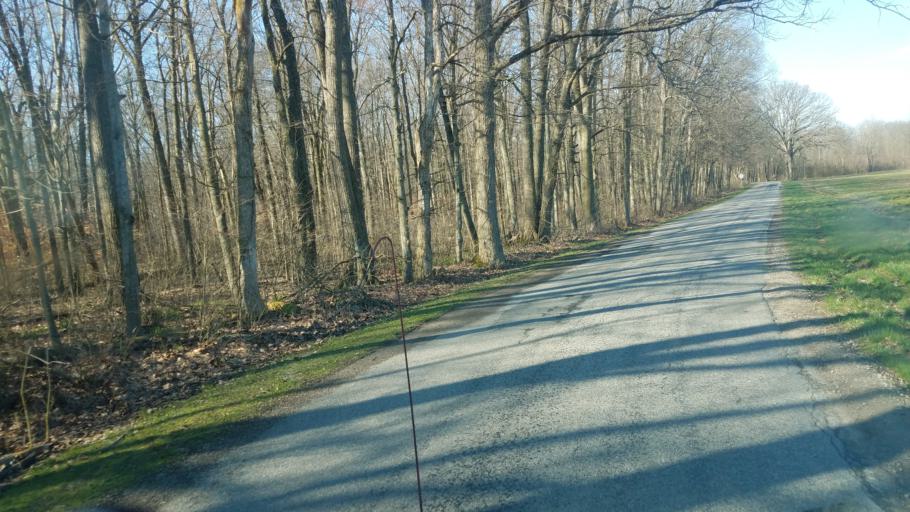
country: US
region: Ohio
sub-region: Delaware County
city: Ashley
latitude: 40.4684
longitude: -83.0572
